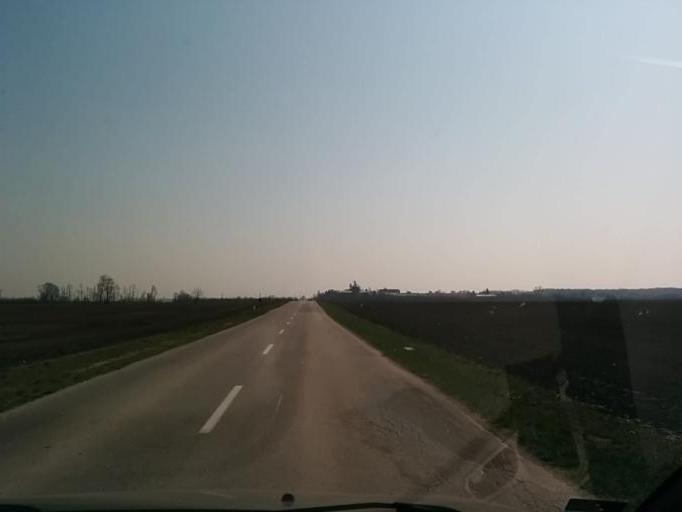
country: SK
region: Trnavsky
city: Sladkovicovo
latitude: 48.2209
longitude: 17.5888
